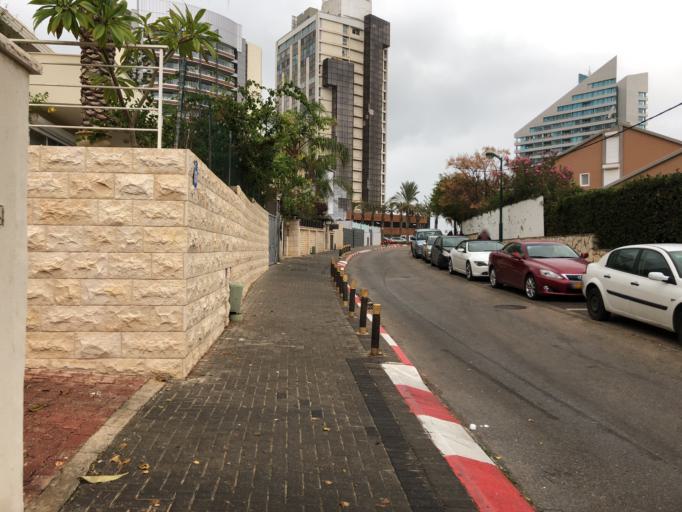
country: IL
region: Tel Aviv
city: Herzliya Pituah
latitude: 32.1708
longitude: 34.8018
